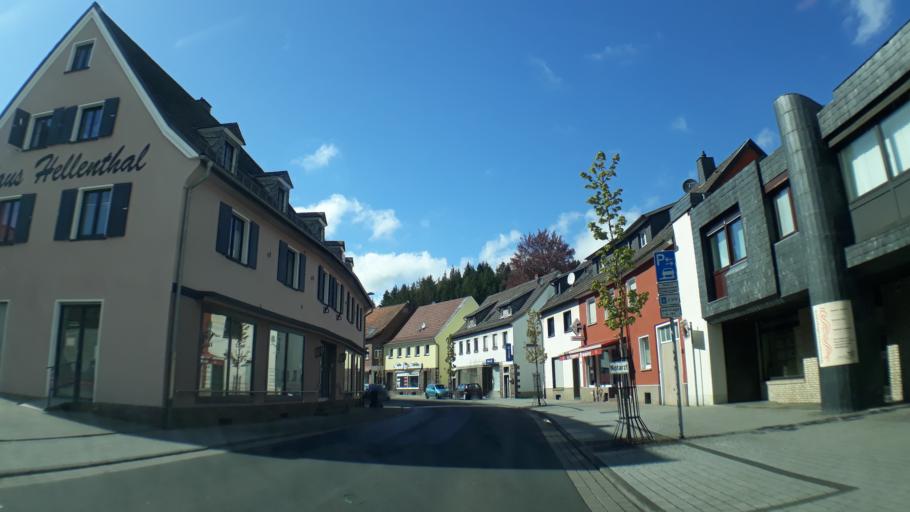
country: DE
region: North Rhine-Westphalia
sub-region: Regierungsbezirk Koln
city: Hellenthal
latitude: 50.4905
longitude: 6.4415
